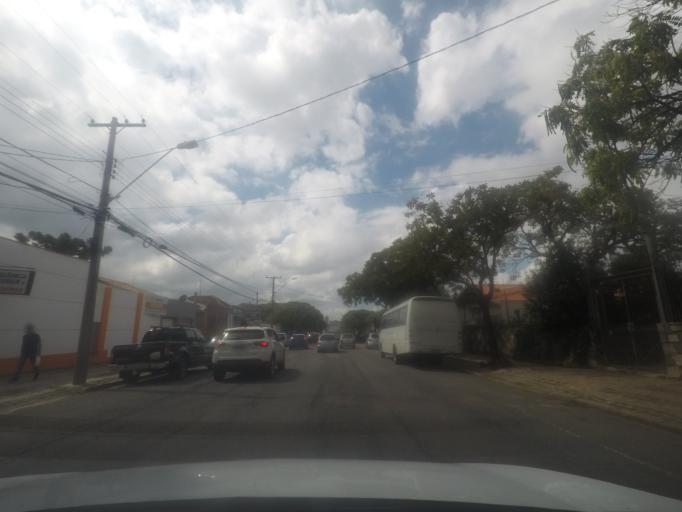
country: BR
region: Parana
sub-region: Curitiba
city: Curitiba
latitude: -25.4496
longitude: -49.2594
